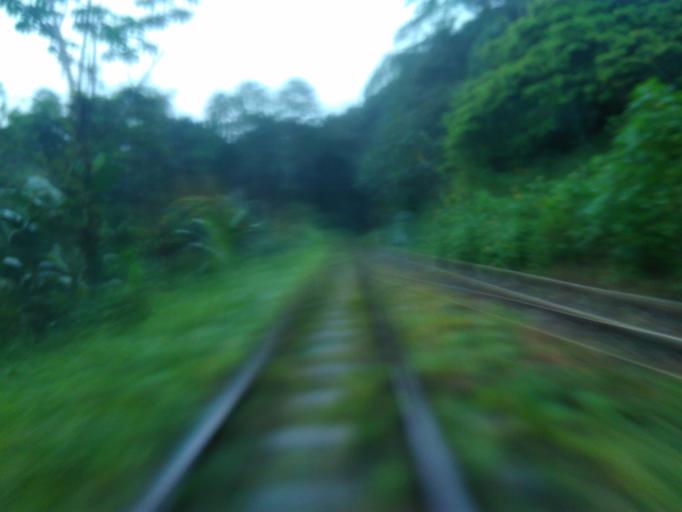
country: CO
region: Valle del Cauca
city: Buenaventura
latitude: 3.8509
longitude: -76.8593
